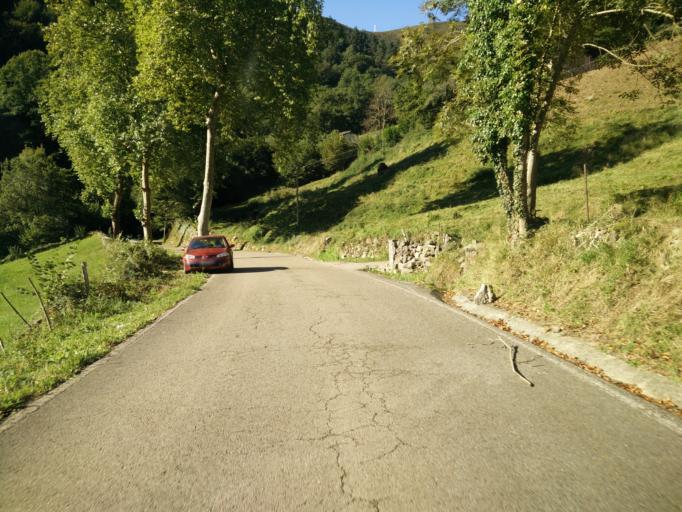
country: ES
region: Cantabria
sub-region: Provincia de Cantabria
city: San Pedro del Romeral
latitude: 43.1248
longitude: -3.8127
